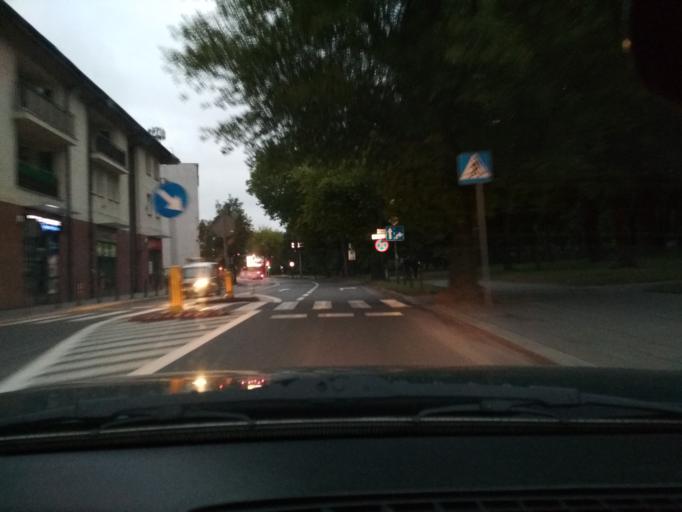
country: PL
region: Silesian Voivodeship
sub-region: Gliwice
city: Gliwice
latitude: 50.2913
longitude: 18.6665
